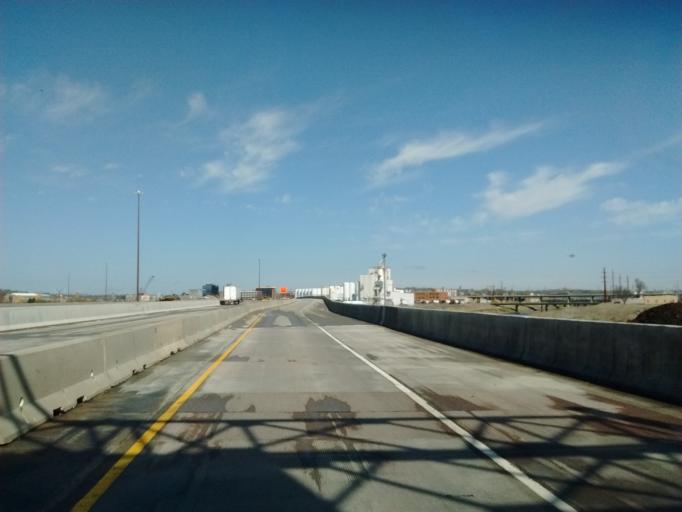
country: US
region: Iowa
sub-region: Woodbury County
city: Sioux City
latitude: 42.4830
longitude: -96.3903
